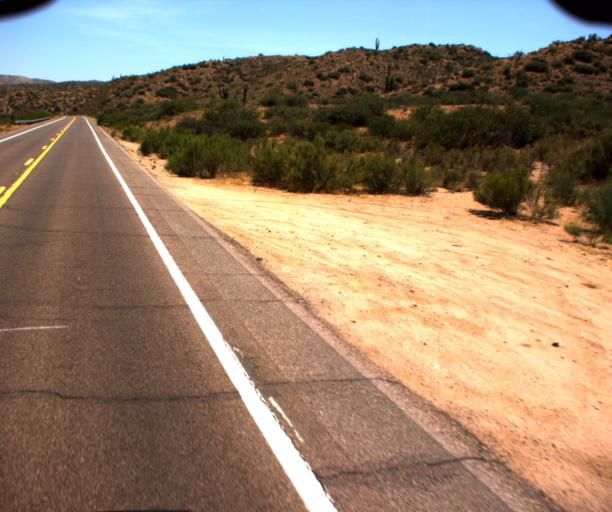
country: US
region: Arizona
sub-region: Gila County
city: Tonto Basin
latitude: 33.7705
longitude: -111.2598
